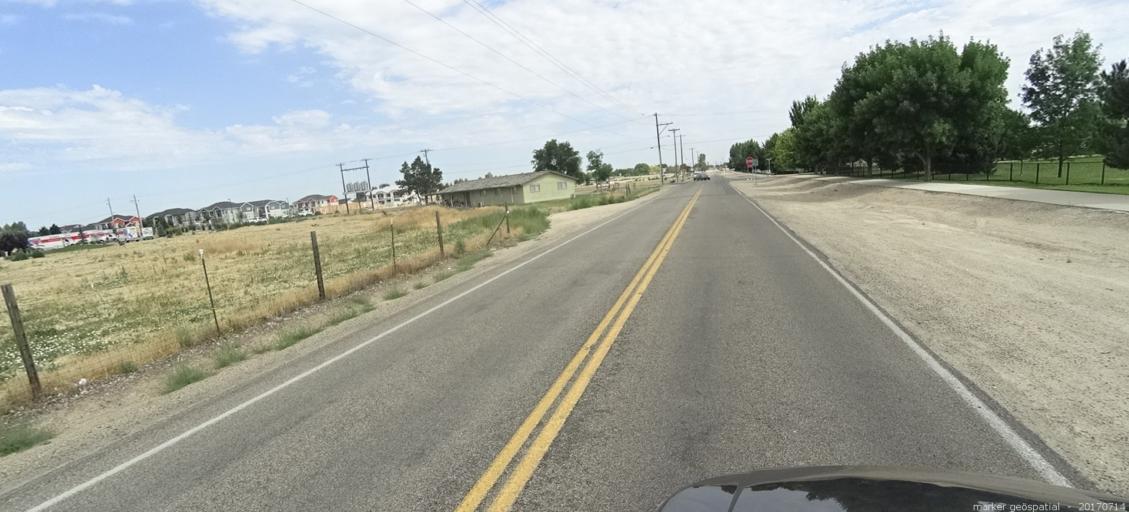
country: US
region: Idaho
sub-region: Ada County
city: Kuna
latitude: 43.5019
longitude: -116.4337
